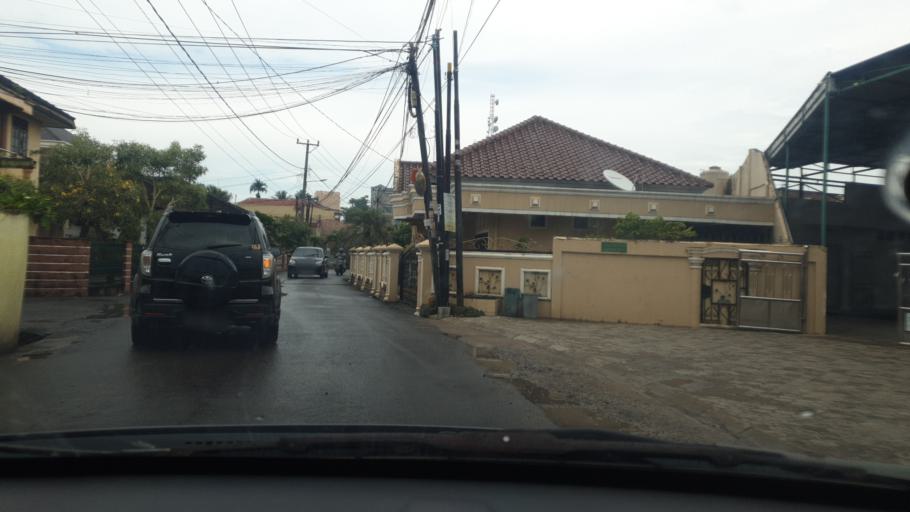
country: ID
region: South Sumatra
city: Palembang
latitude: -2.9751
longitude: 104.7235
